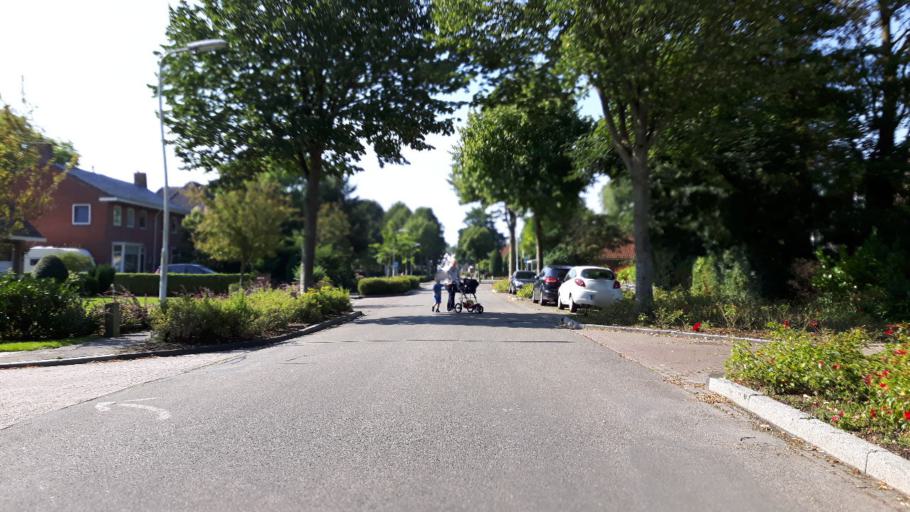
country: NL
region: Friesland
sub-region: Gemeente Ferwerderadiel
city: Ferwert
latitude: 53.3409
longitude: 5.8289
